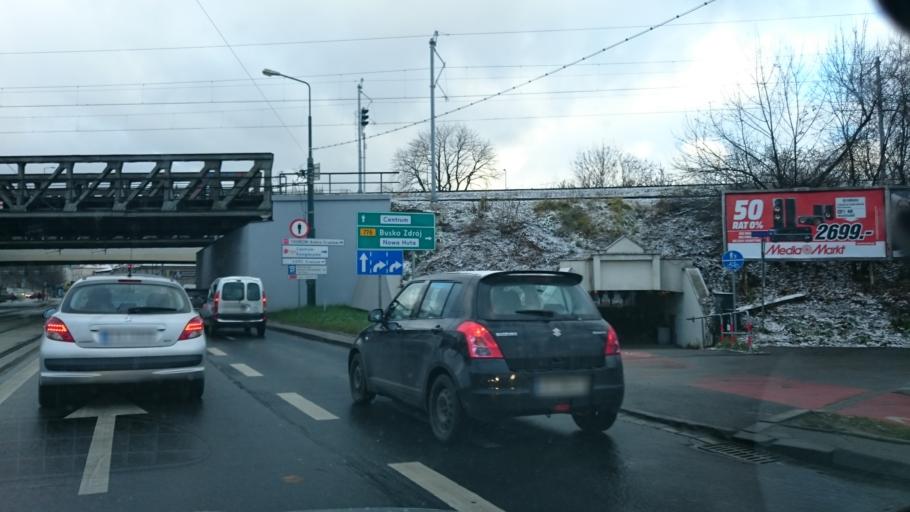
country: PL
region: Lesser Poland Voivodeship
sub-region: Krakow
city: Krakow
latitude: 50.0409
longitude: 19.9624
